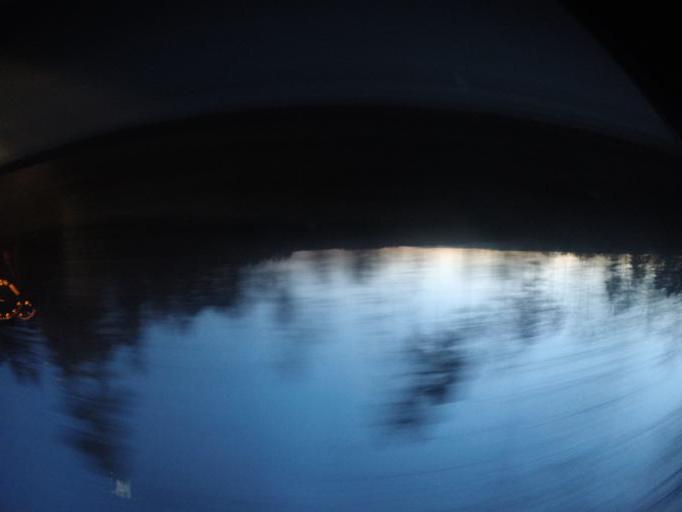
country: SE
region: Vaestmanland
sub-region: Arboga Kommun
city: Arboga
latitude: 59.4103
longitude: 15.7371
